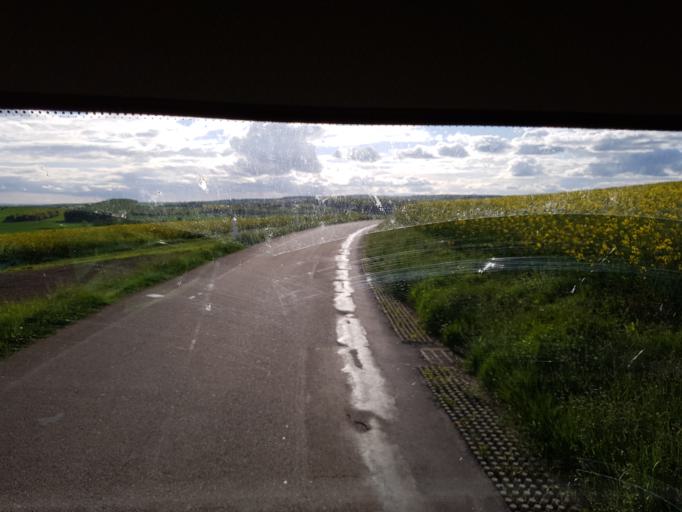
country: FR
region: Bourgogne
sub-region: Departement de l'Yonne
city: Saint-Florentin
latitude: 48.0633
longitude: 3.7206
